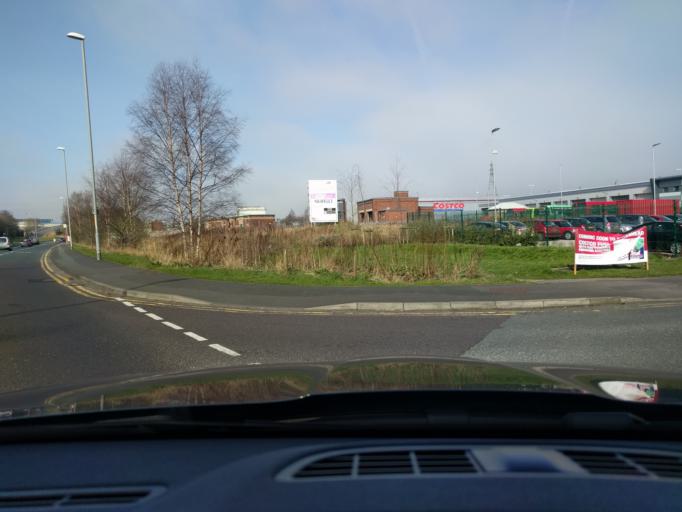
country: GB
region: England
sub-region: Newcastle upon Tyne
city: Benwell
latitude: 54.9586
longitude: -1.6566
